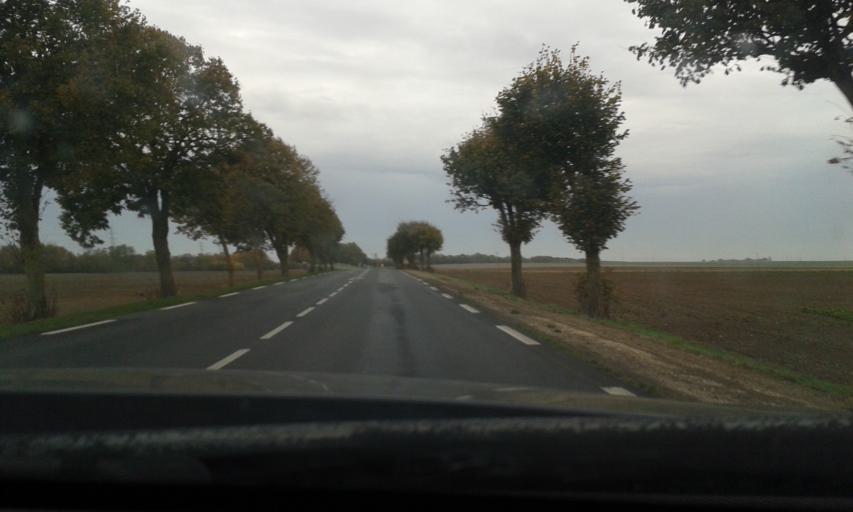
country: FR
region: Centre
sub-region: Departement d'Eure-et-Loir
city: Baigneaux
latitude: 48.1240
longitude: 1.8565
